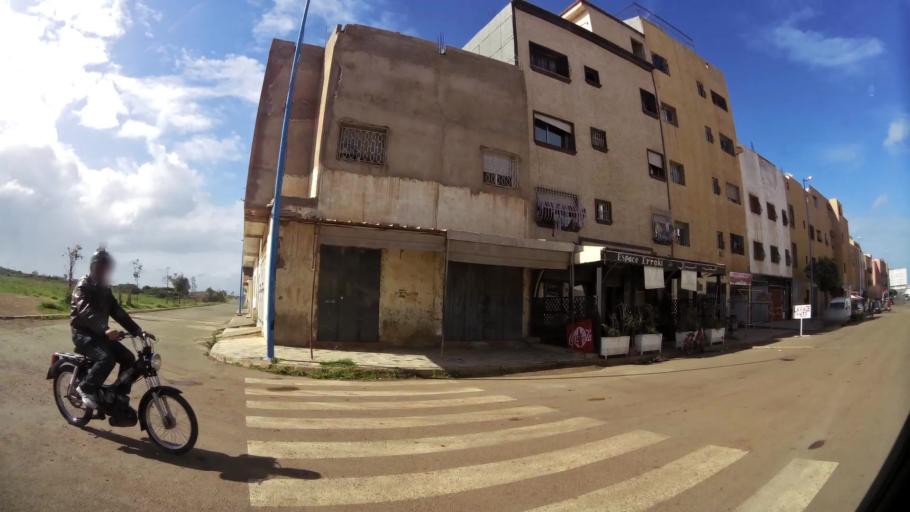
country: MA
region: Grand Casablanca
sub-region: Casablanca
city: Casablanca
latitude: 33.5641
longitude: -7.6962
